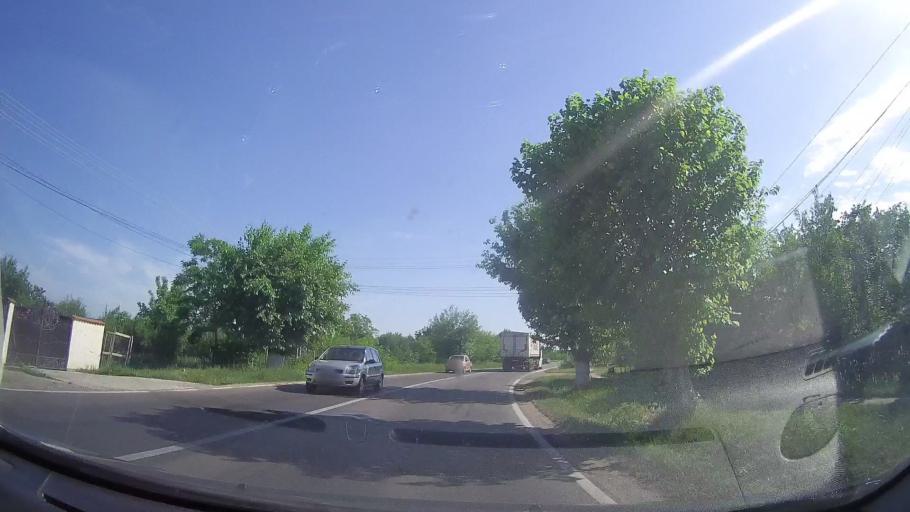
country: RO
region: Prahova
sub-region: Comuna Magurele
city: Magurele
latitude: 45.0891
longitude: 26.0368
